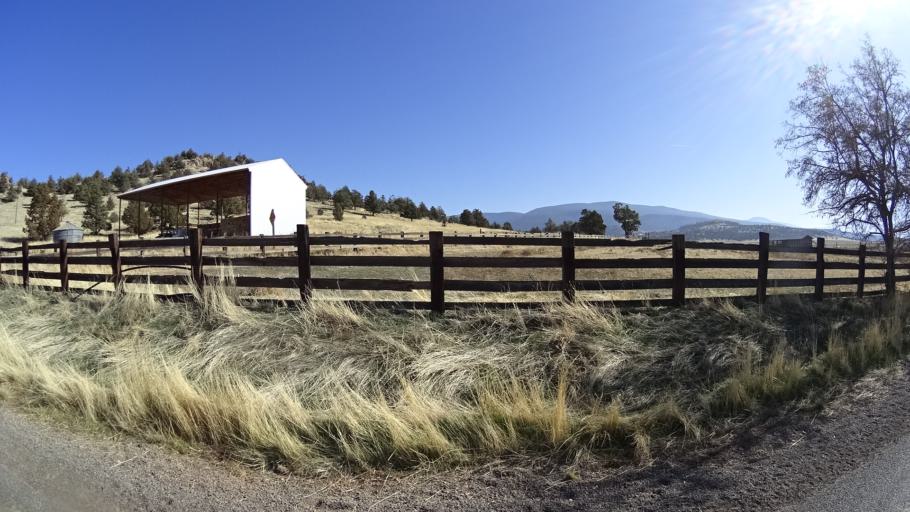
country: US
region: California
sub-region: Siskiyou County
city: Montague
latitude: 41.6887
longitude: -122.3698
